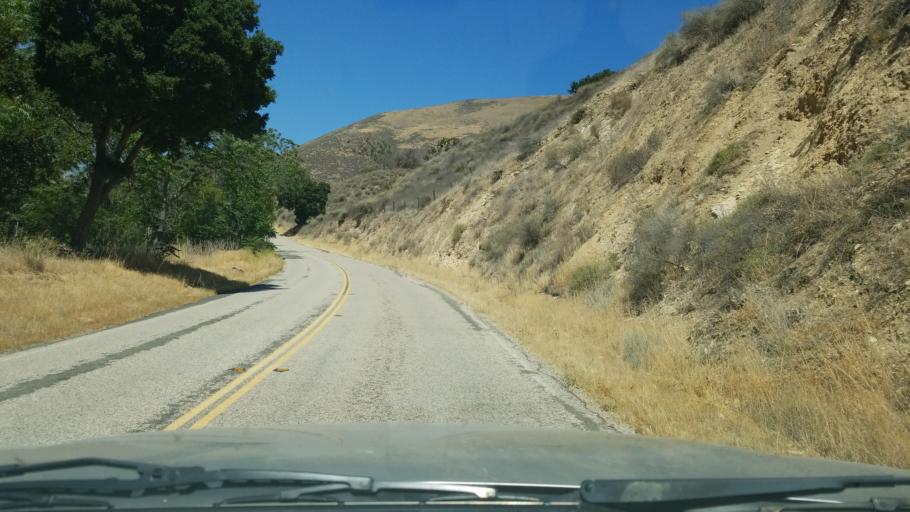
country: US
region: California
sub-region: Monterey County
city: Greenfield
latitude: 36.2711
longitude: -121.3406
